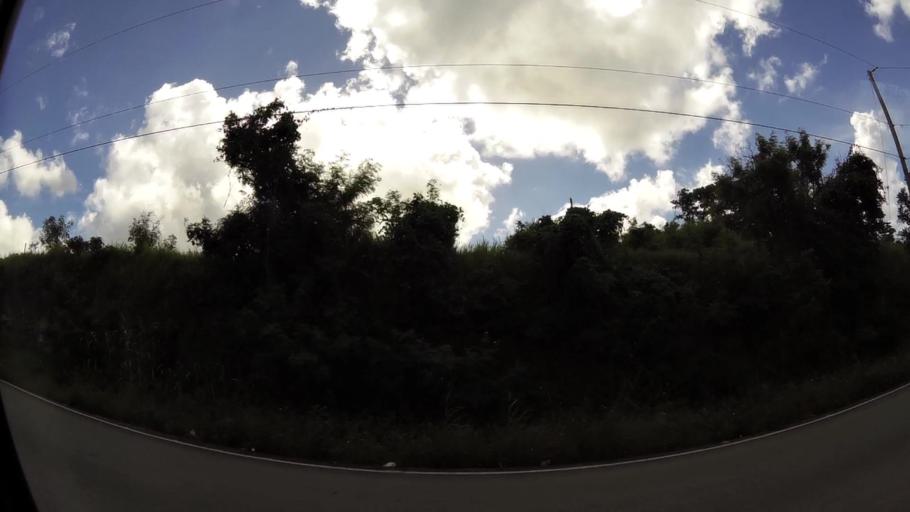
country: BB
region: Saint James
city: Holetown
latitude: 13.1994
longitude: -59.6184
